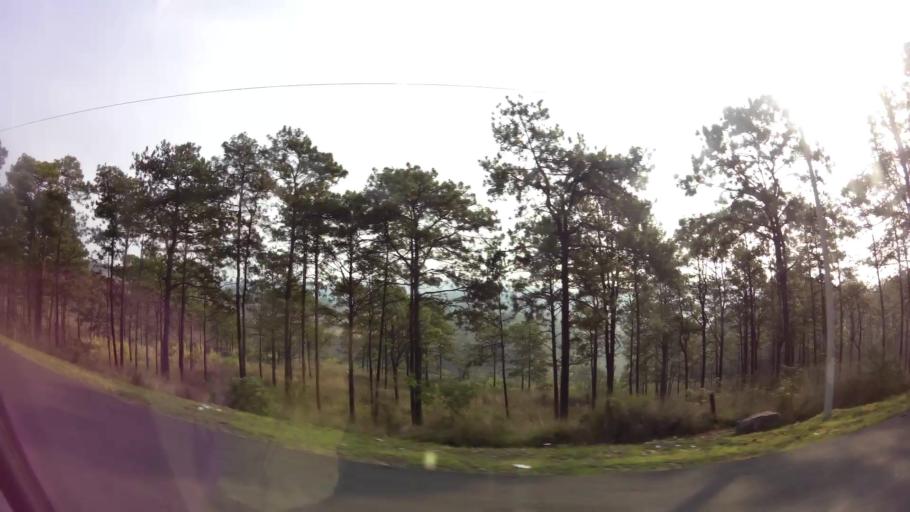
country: HN
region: Francisco Morazan
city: Zambrano
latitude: 14.2520
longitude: -87.3814
